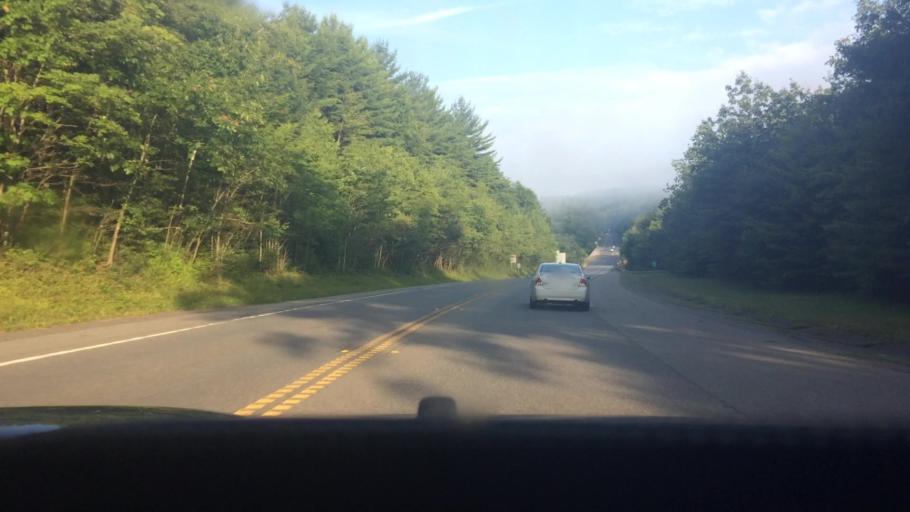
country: US
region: Massachusetts
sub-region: Franklin County
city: Erving
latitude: 42.5968
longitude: -72.3539
